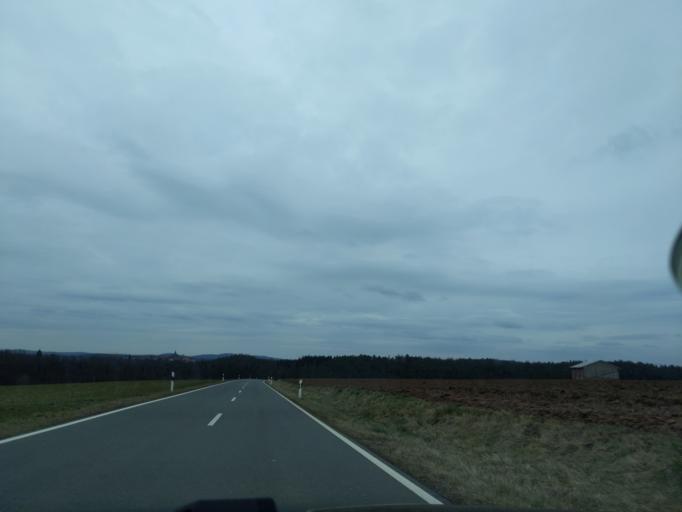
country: DE
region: Hesse
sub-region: Regierungsbezirk Kassel
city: Bad Arolsen
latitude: 51.3255
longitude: 9.0621
